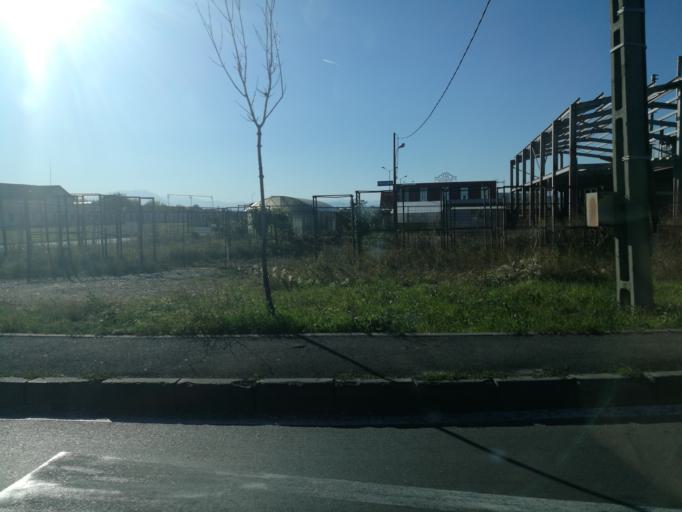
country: RO
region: Brasov
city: Brasov
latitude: 45.6733
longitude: 25.5896
